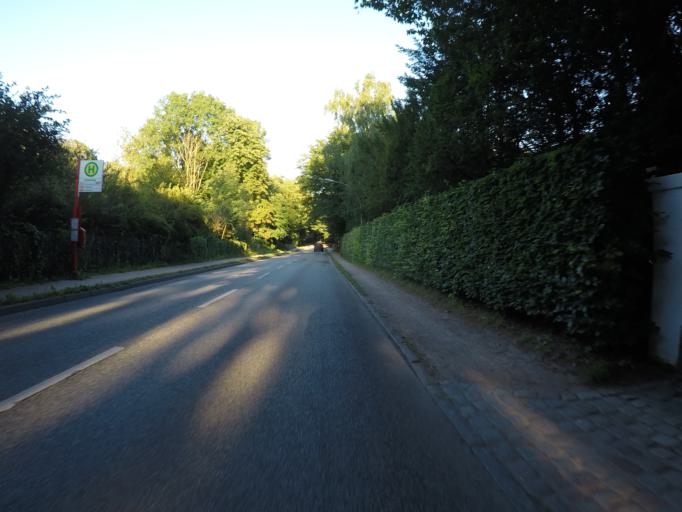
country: DE
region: Hamburg
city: Bergstedt
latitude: 53.6837
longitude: 10.1150
